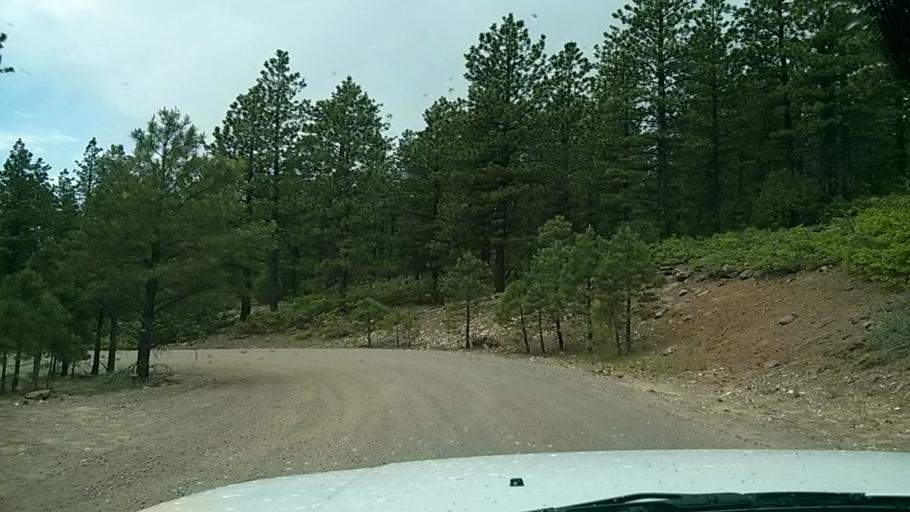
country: US
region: Utah
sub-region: Wayne County
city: Loa
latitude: 37.9459
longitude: -111.6590
